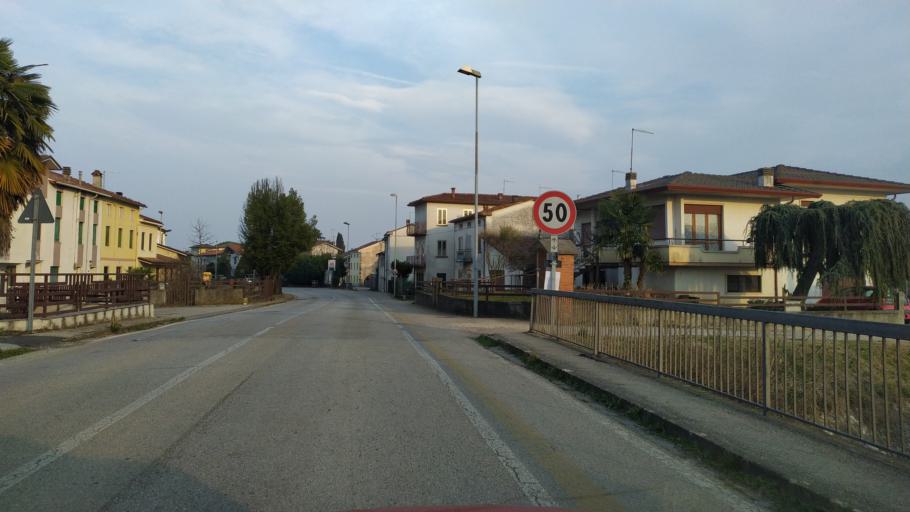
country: IT
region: Veneto
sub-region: Provincia di Vicenza
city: Marano Vicentino
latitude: 45.6911
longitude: 11.4226
